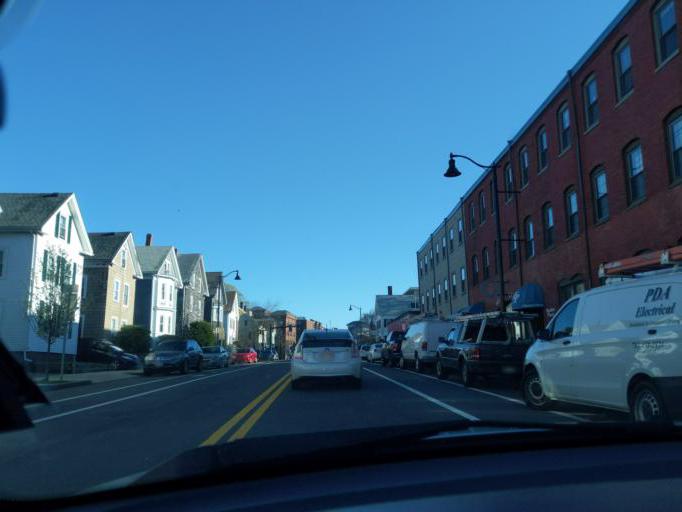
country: US
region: Massachusetts
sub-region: Essex County
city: Beverly
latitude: 42.5423
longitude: -70.8850
